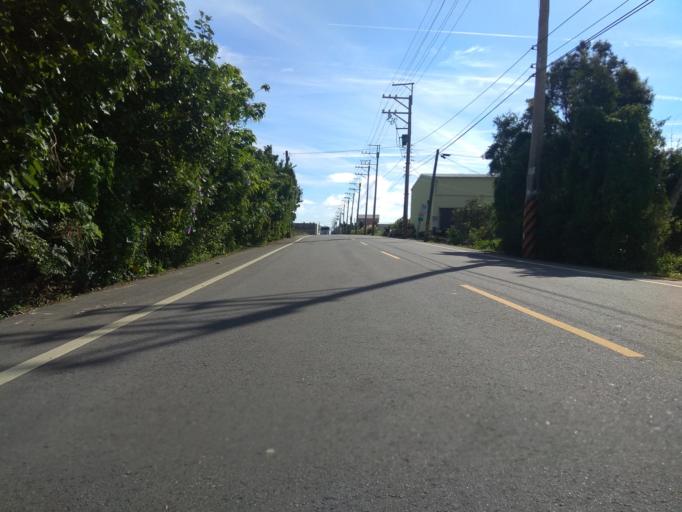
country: TW
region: Taiwan
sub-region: Hsinchu
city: Zhubei
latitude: 25.0096
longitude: 121.0413
